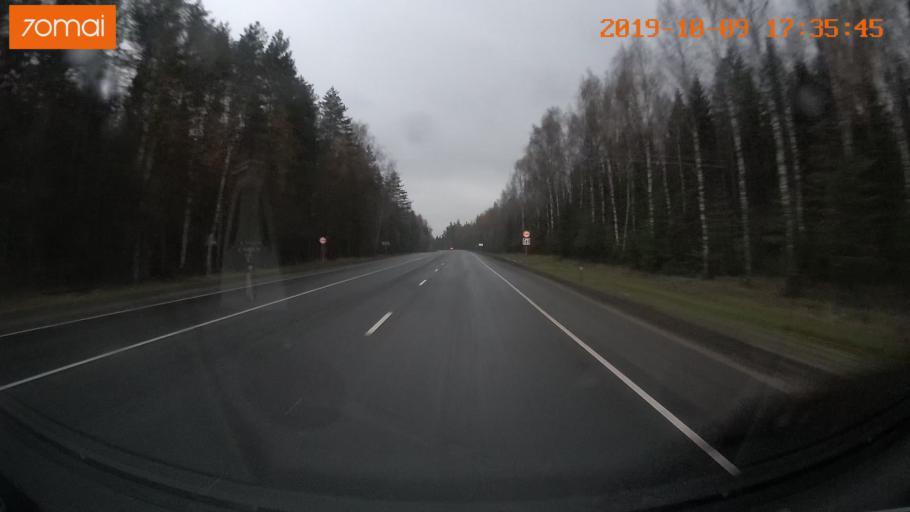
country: RU
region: Ivanovo
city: Bogorodskoye
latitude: 57.0886
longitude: 40.9999
